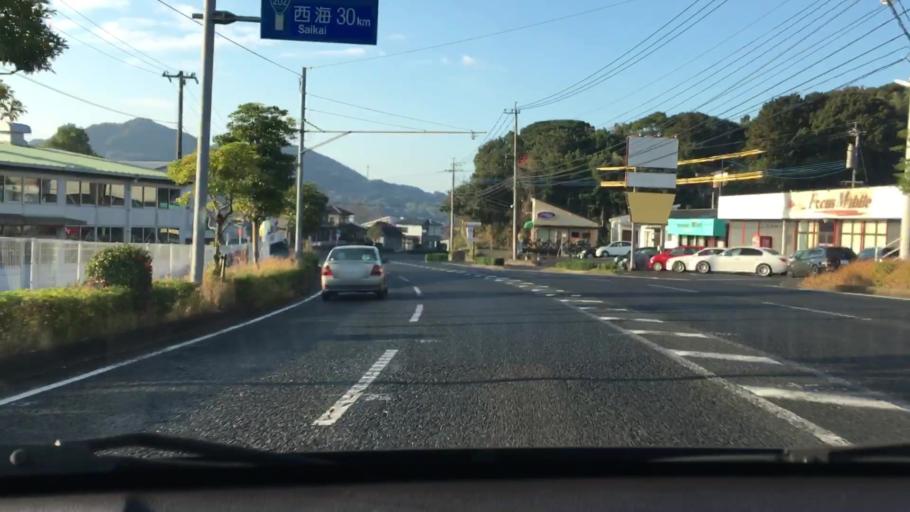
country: JP
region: Nagasaki
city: Sasebo
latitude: 33.1155
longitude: 129.7909
